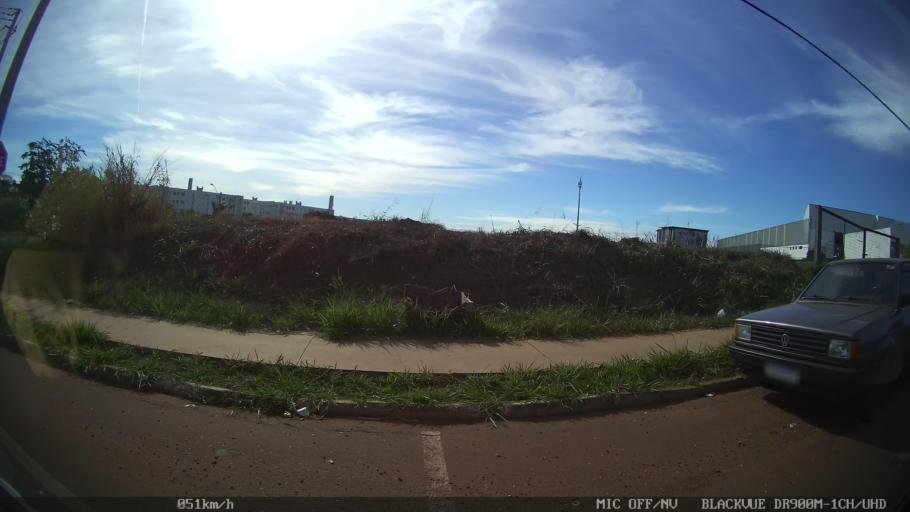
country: BR
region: Sao Paulo
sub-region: Sao Jose Do Rio Preto
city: Sao Jose do Rio Preto
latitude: -20.7989
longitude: -49.3327
